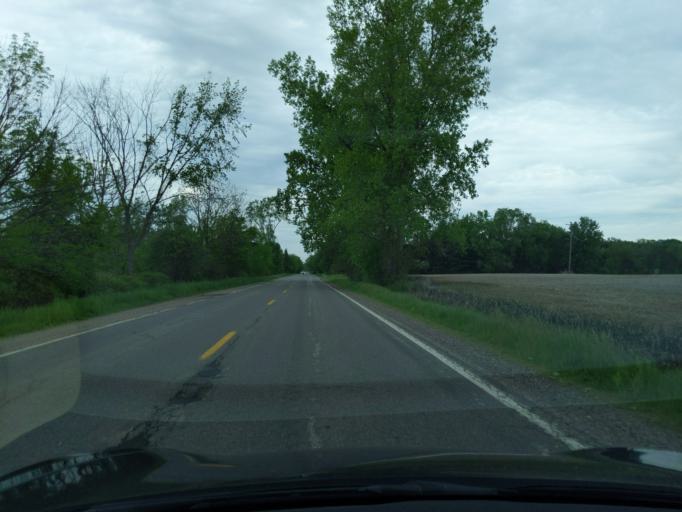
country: US
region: Michigan
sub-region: Ingham County
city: Mason
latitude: 42.6063
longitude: -84.3580
